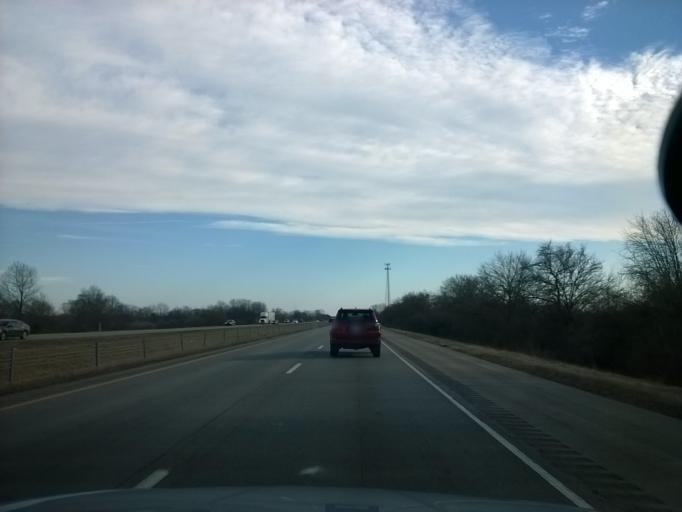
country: US
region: Indiana
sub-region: Johnson County
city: Edinburgh
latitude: 39.4279
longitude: -85.9746
